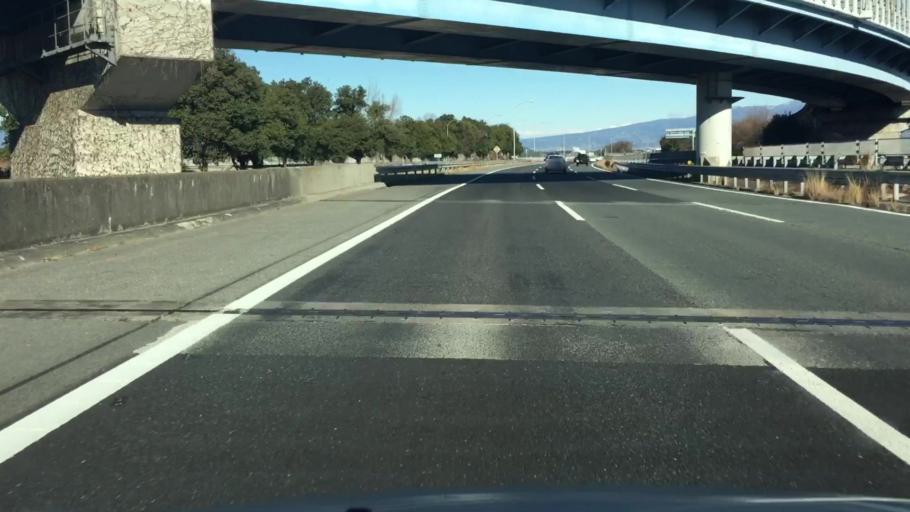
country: JP
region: Gunma
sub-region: Sawa-gun
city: Tamamura
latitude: 36.2736
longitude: 139.0954
